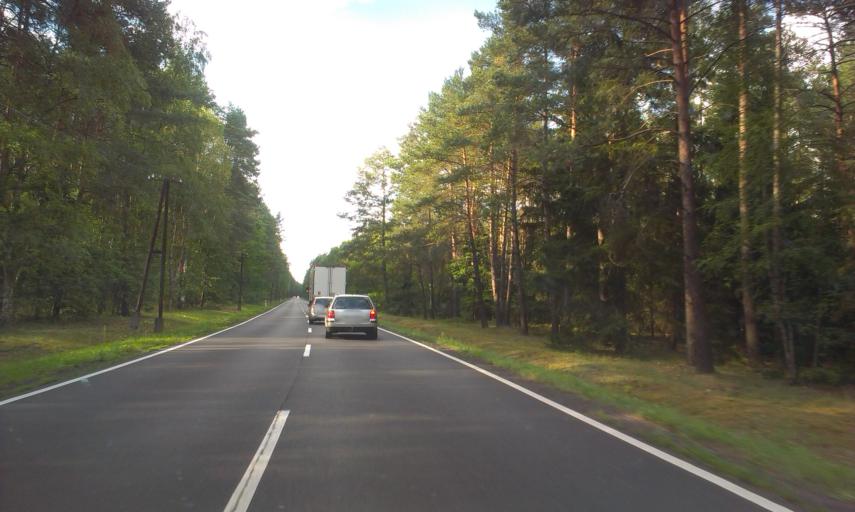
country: PL
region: Greater Poland Voivodeship
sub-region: Powiat zlotowski
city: Tarnowka
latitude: 53.2796
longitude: 16.7825
